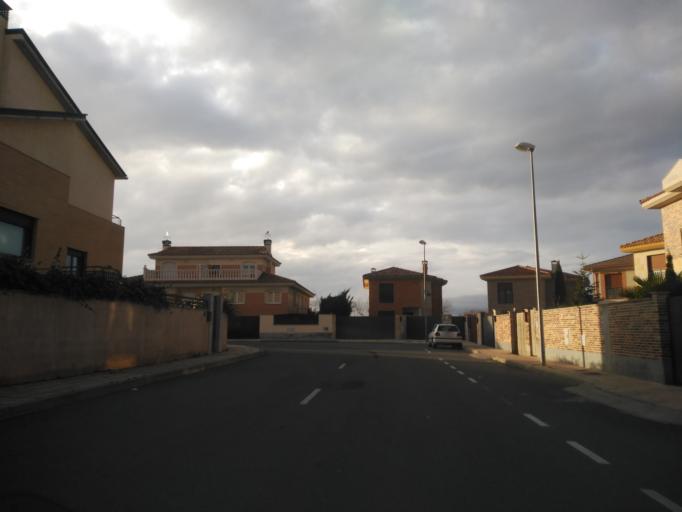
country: ES
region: Castille and Leon
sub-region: Provincia de Salamanca
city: Santa Marta de Tormes
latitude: 40.9323
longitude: -5.6273
